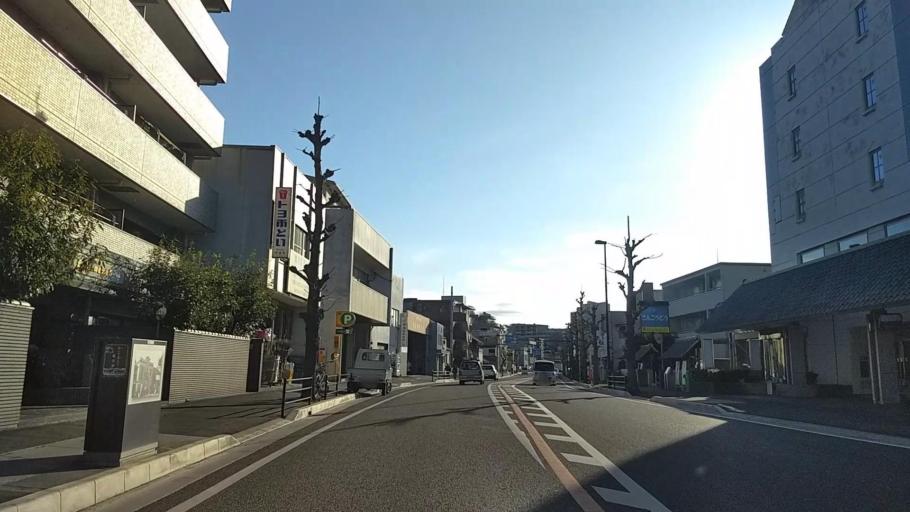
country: JP
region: Kanagawa
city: Fujisawa
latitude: 35.3473
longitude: 139.4839
